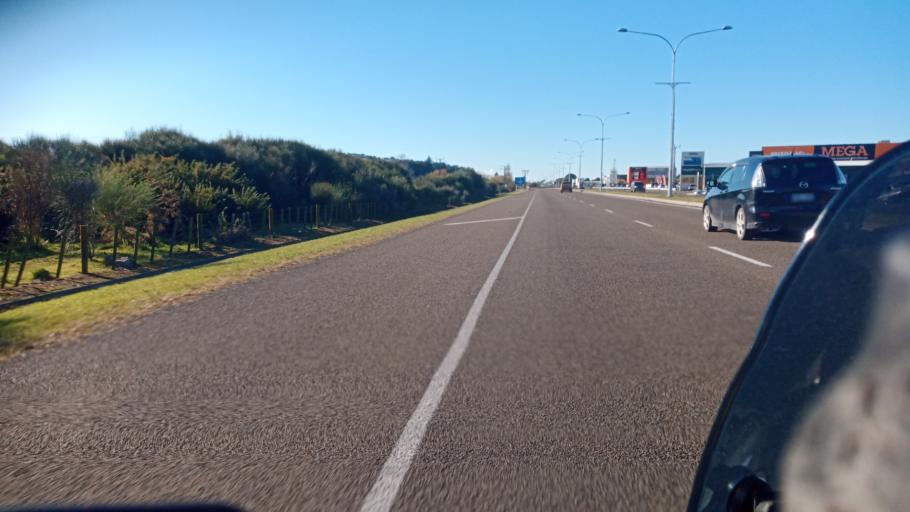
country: NZ
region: Hawke's Bay
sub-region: Napier City
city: Napier
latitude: -39.4962
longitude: 176.8811
